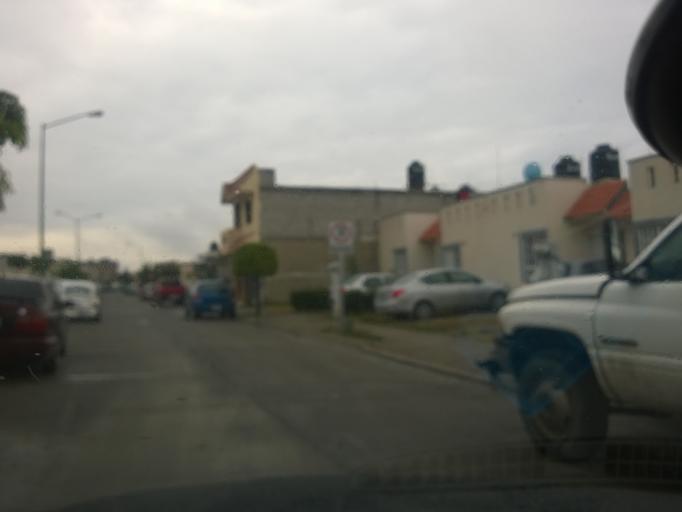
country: MX
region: Guanajuato
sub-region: Leon
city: La Ermita
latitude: 21.1565
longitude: -101.7467
